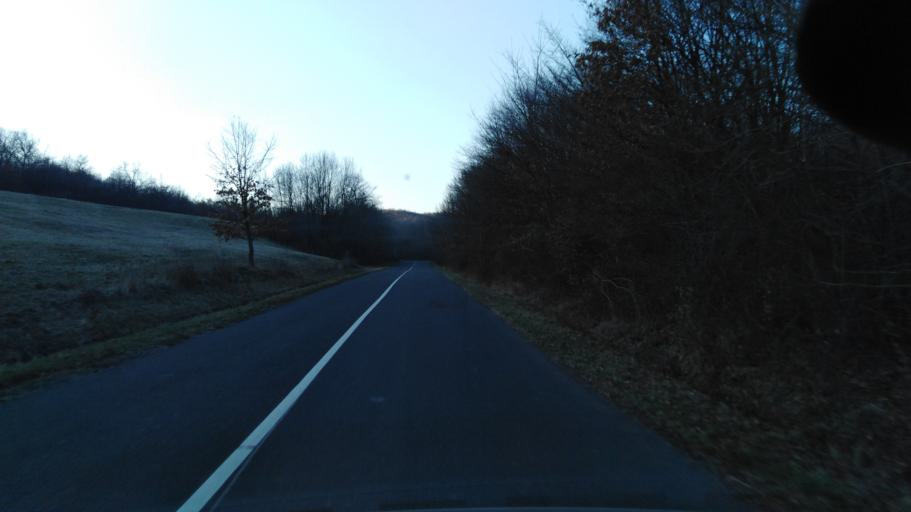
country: HU
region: Nograd
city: Kazar
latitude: 48.0633
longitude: 19.8272
